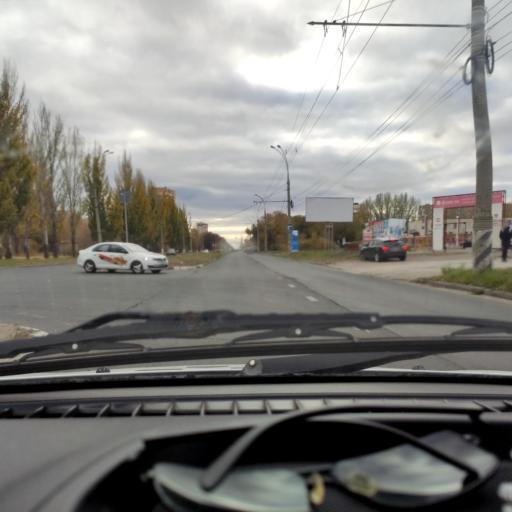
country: RU
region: Samara
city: Tol'yatti
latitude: 53.5405
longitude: 49.2789
